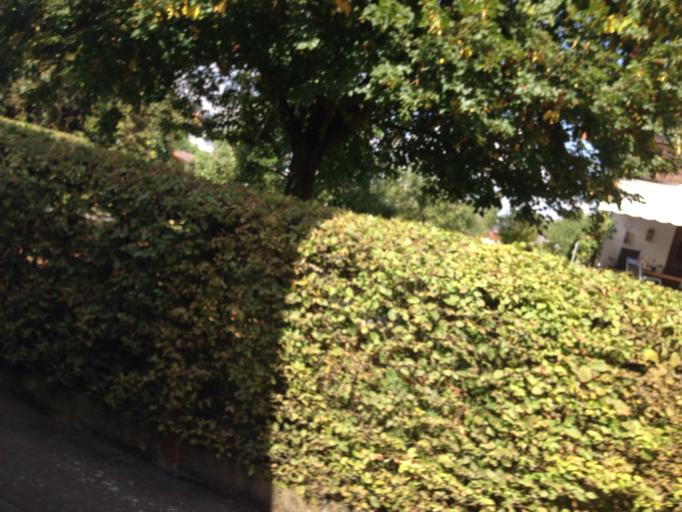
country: DE
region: Hesse
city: Allendorf an der Lahn
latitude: 50.5387
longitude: 8.6239
